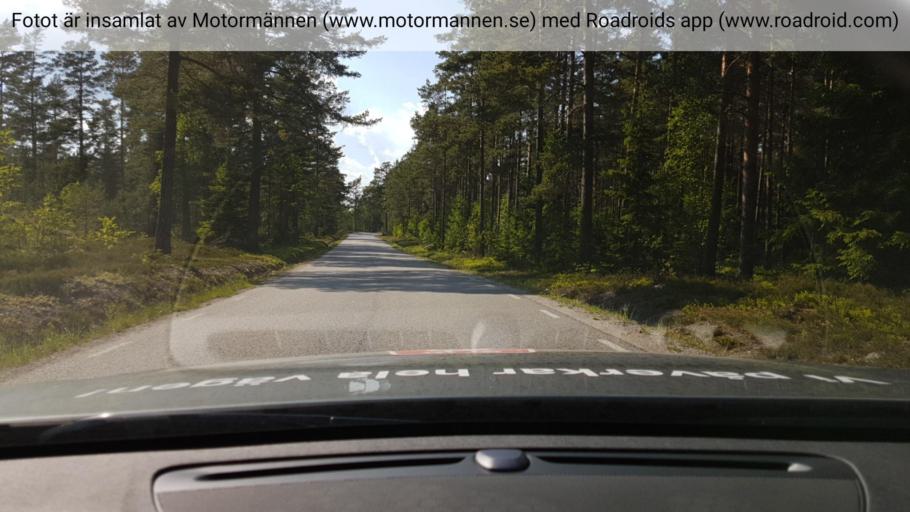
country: SE
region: Stockholm
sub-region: Varmdo Kommun
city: Mortnas
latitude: 59.2550
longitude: 18.4471
